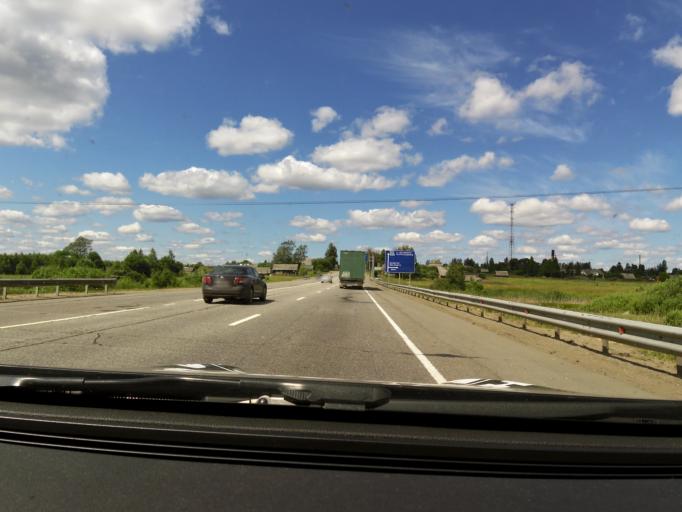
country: RU
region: Tverskaya
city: Kuzhenkino
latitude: 57.7578
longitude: 33.9635
